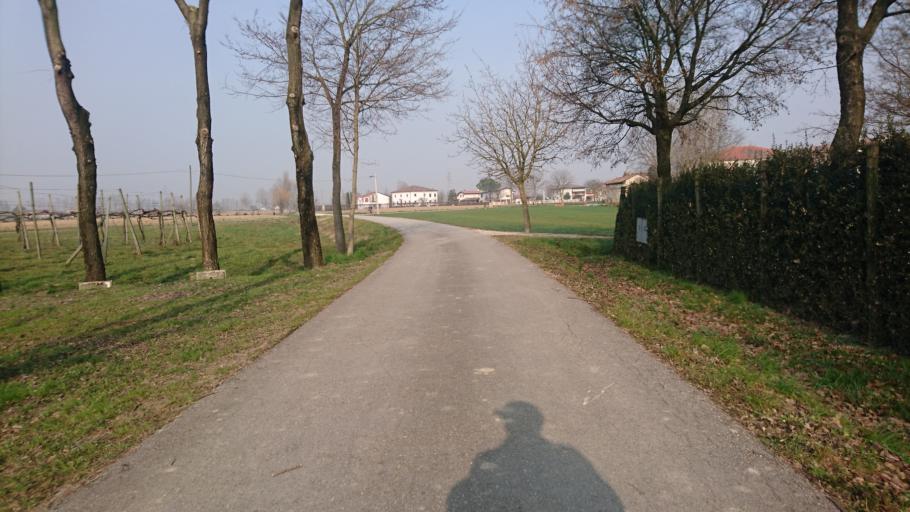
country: IT
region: Veneto
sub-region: Provincia di Padova
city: Veggiano
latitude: 45.4366
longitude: 11.7152
